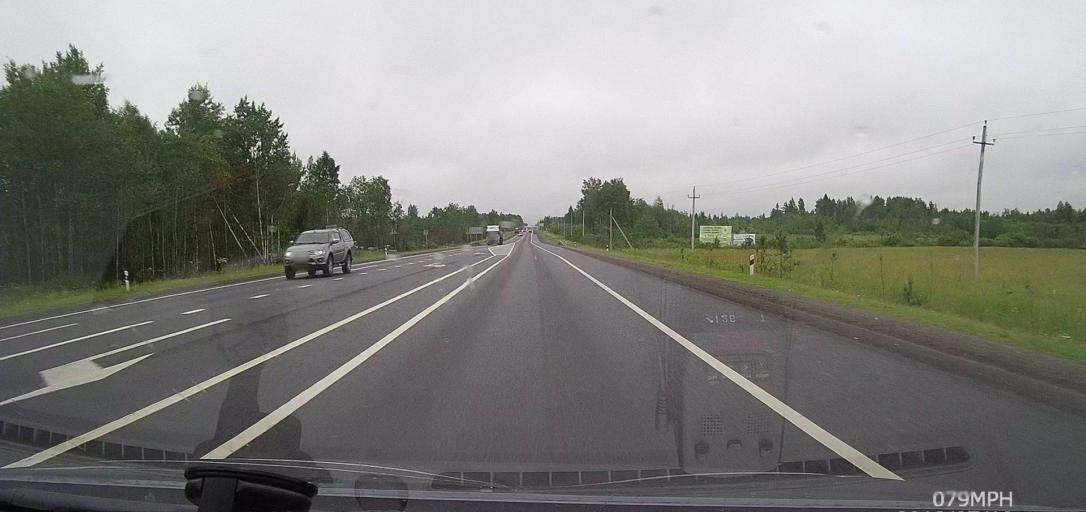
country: RU
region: Leningrad
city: Staraya Ladoga
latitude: 60.0005
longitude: 32.1133
